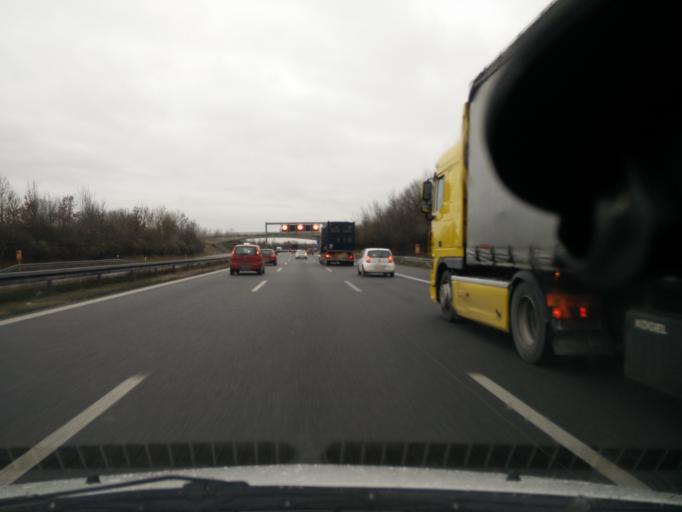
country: DE
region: Bavaria
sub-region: Upper Bavaria
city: Karlsfeld
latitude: 48.2143
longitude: 11.5015
